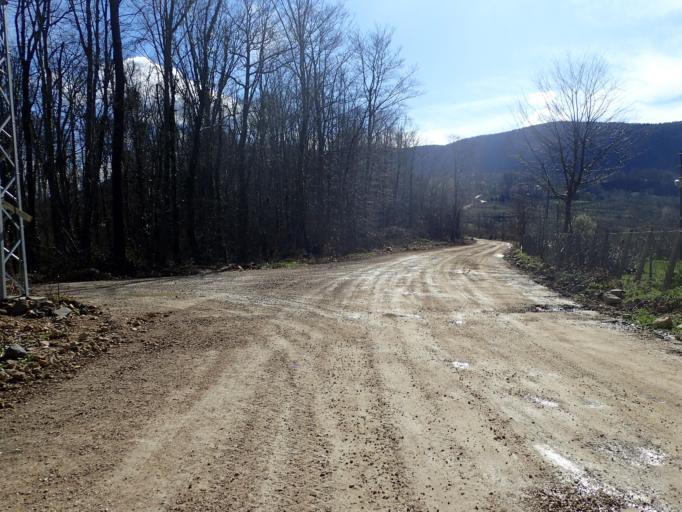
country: TR
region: Ordu
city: Kumru
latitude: 40.9335
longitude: 37.2555
